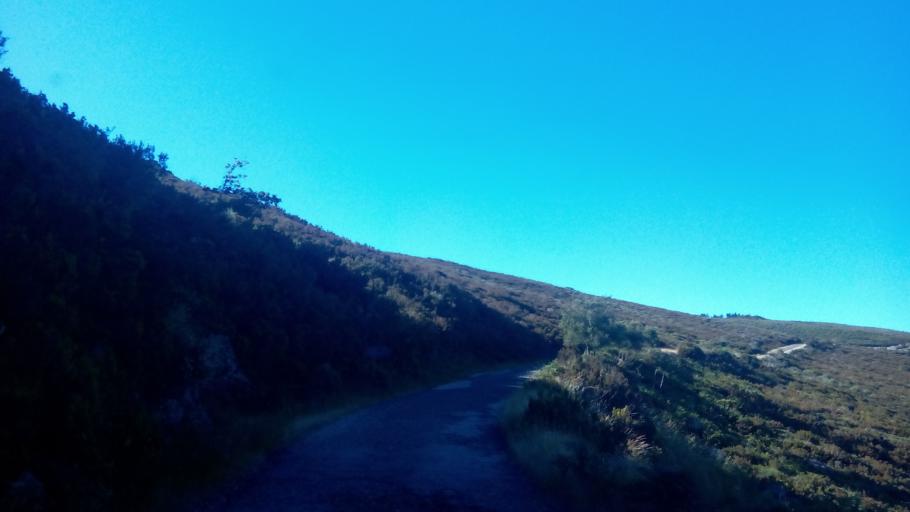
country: PT
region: Vila Real
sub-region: Mesao Frio
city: Mesao Frio
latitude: 41.2613
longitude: -7.8975
